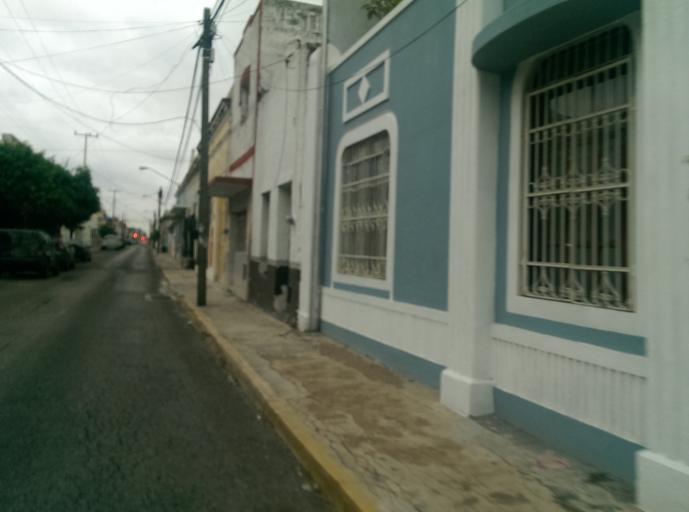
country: MX
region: Yucatan
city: Merida
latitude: 20.9742
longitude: -89.6258
